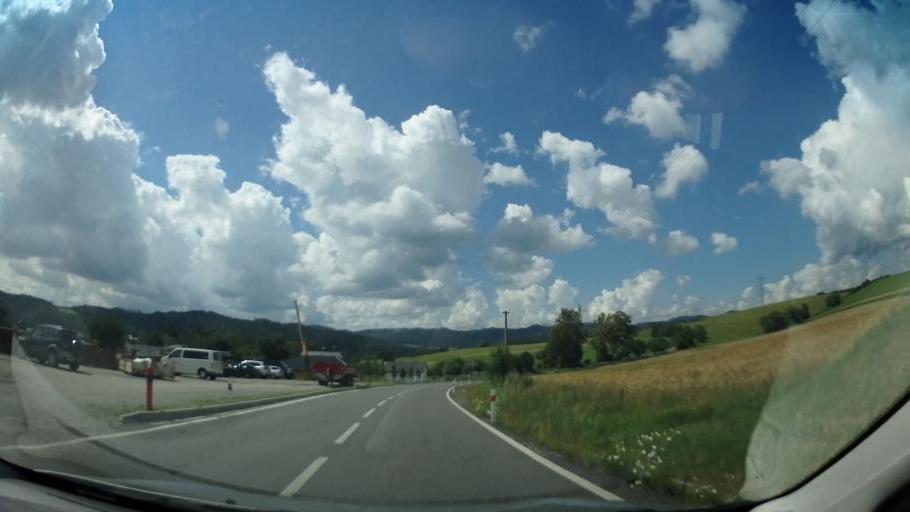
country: CZ
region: Olomoucky
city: Zabreh
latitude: 49.8797
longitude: 16.8589
